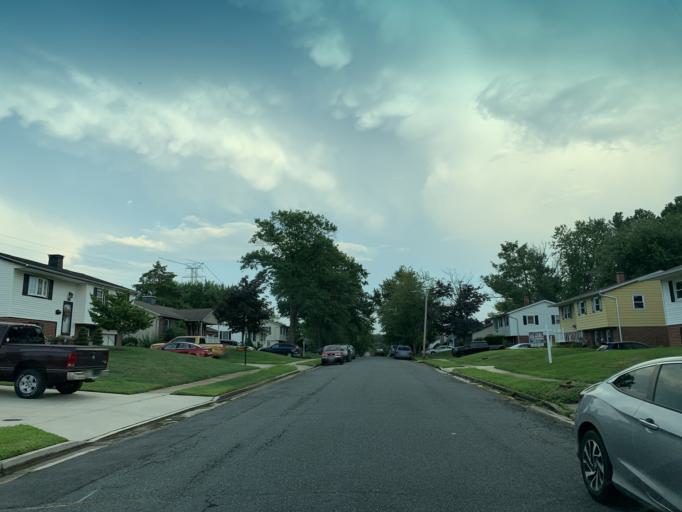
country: US
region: Maryland
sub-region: Harford County
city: Joppatowne
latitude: 39.4094
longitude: -76.3475
